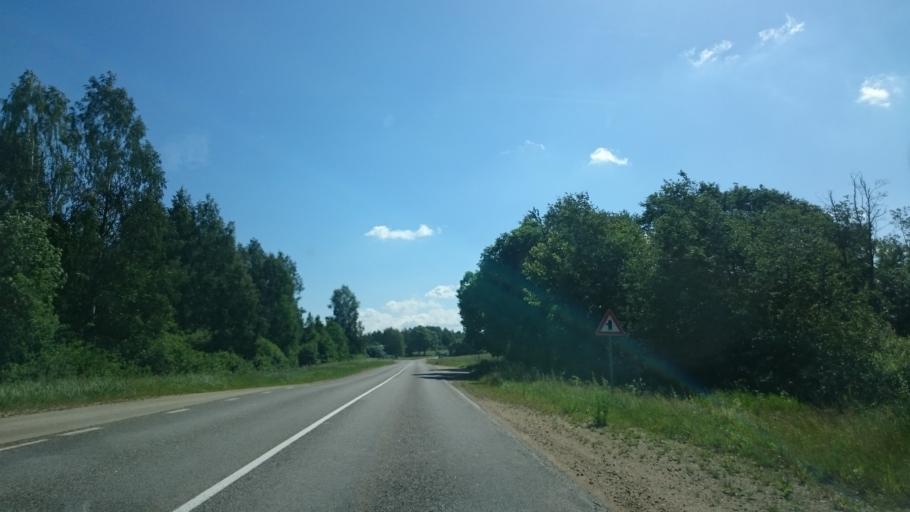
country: LV
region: Ludzas Rajons
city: Ludza
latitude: 56.5076
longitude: 27.7772
